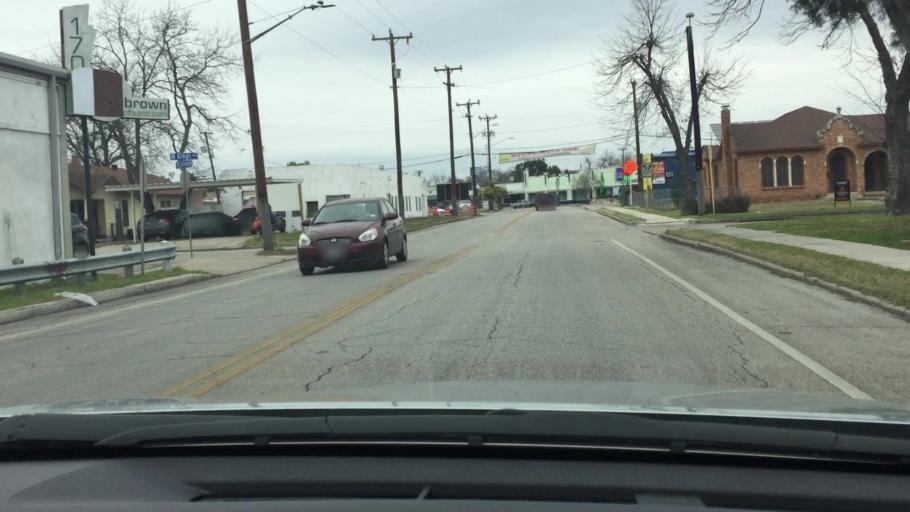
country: US
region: Texas
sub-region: Bexar County
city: Balcones Heights
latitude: 29.4599
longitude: -98.5231
